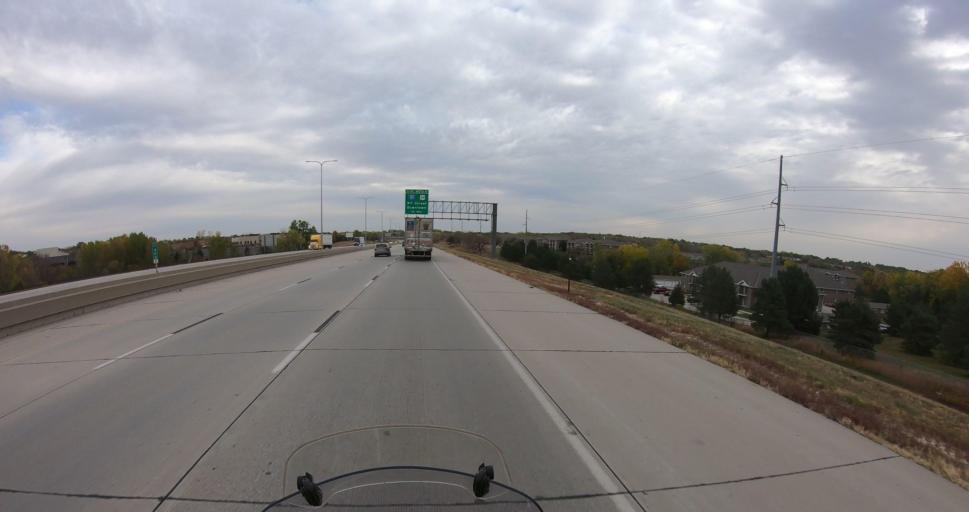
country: US
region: Nebraska
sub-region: Lancaster County
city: Lincoln
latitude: 40.8519
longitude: -96.7230
